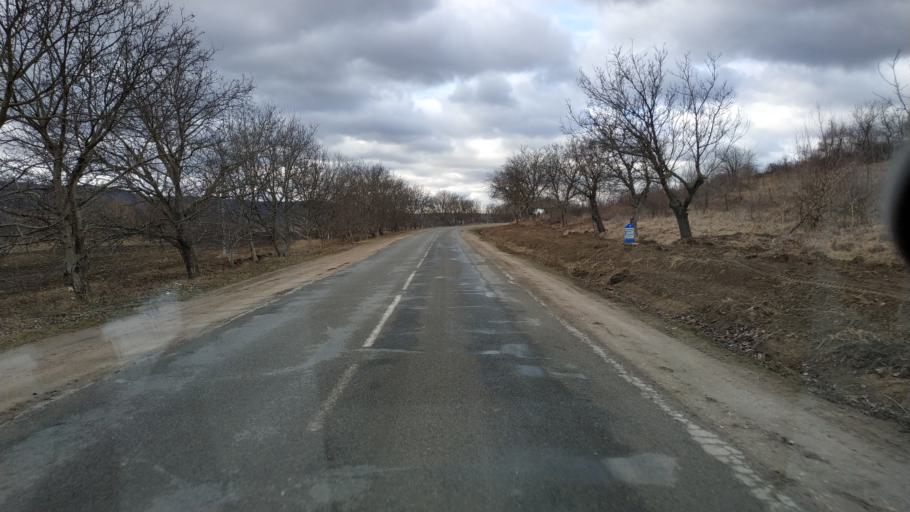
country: MD
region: Stinga Nistrului
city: Bucovat
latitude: 47.1750
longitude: 28.4573
